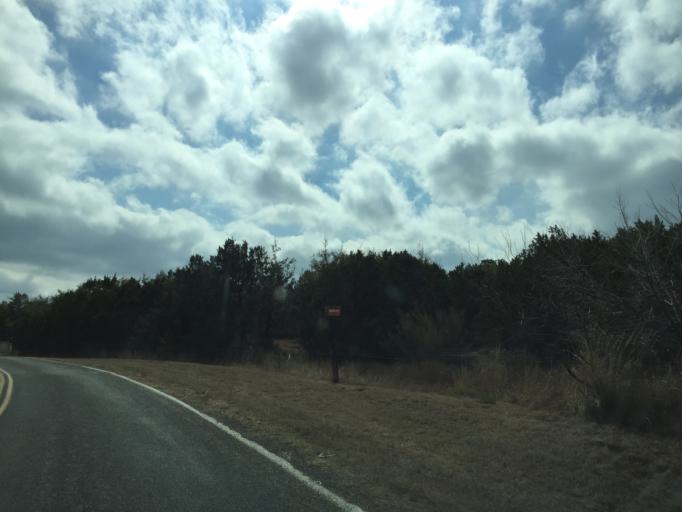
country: US
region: Texas
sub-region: Travis County
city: Briarcliff
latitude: 30.3759
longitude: -98.0931
